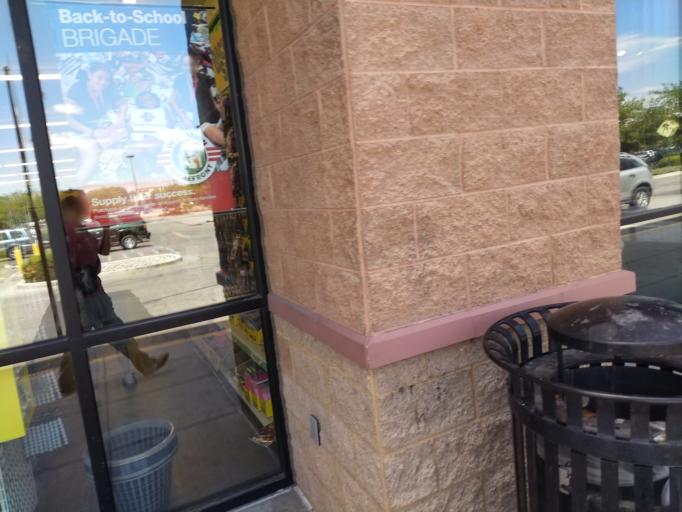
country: US
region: Colorado
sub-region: Mesa County
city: Grand Junction
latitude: 39.0772
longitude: -108.5837
